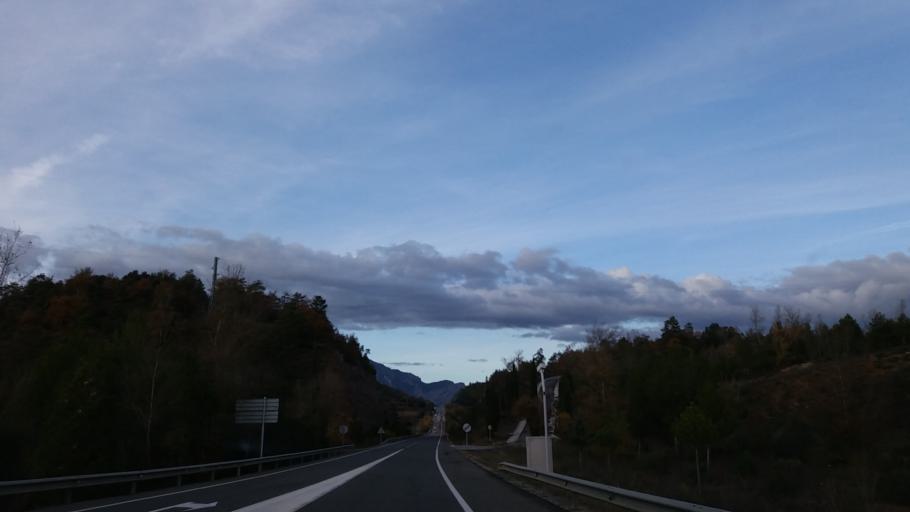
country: ES
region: Catalonia
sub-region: Provincia de Lleida
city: Tiurana
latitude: 42.0075
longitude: 1.2939
